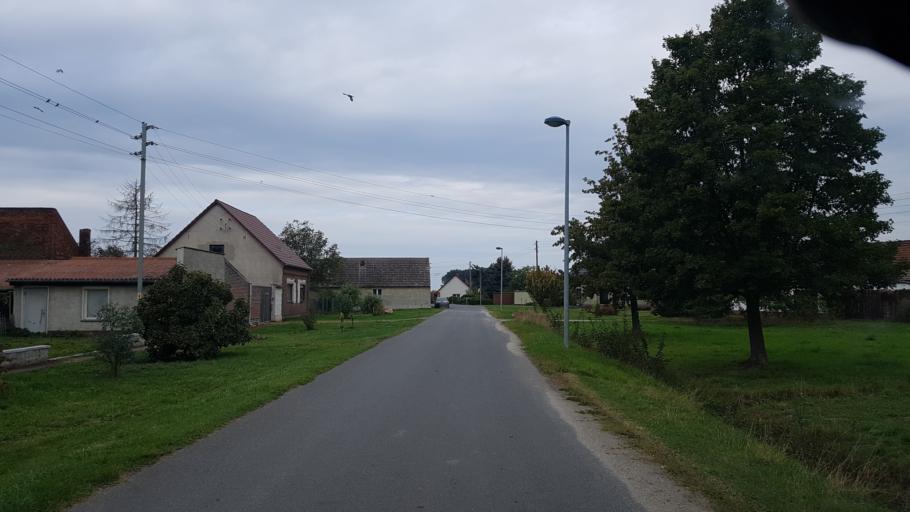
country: DE
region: Brandenburg
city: Schonewalde
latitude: 51.6602
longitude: 13.5860
